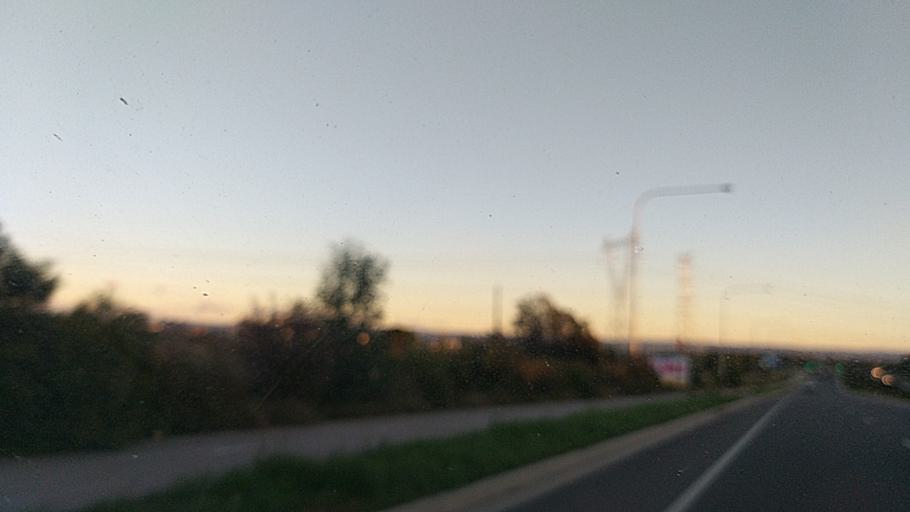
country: AU
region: New South Wales
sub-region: Blacktown
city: Hassall Grove
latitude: -33.6950
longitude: 150.8291
